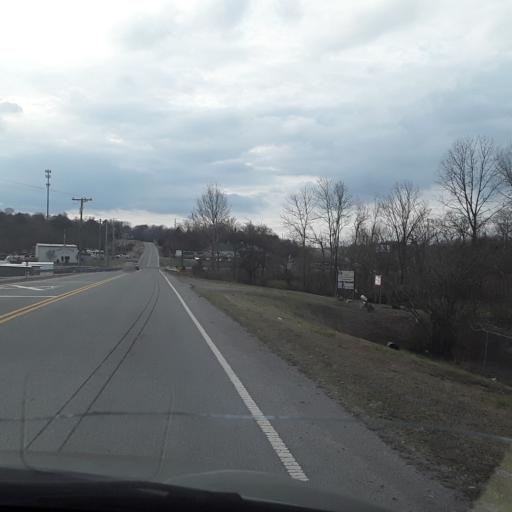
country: US
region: Tennessee
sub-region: Wilson County
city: Mount Juliet
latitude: 36.2305
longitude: -86.4258
